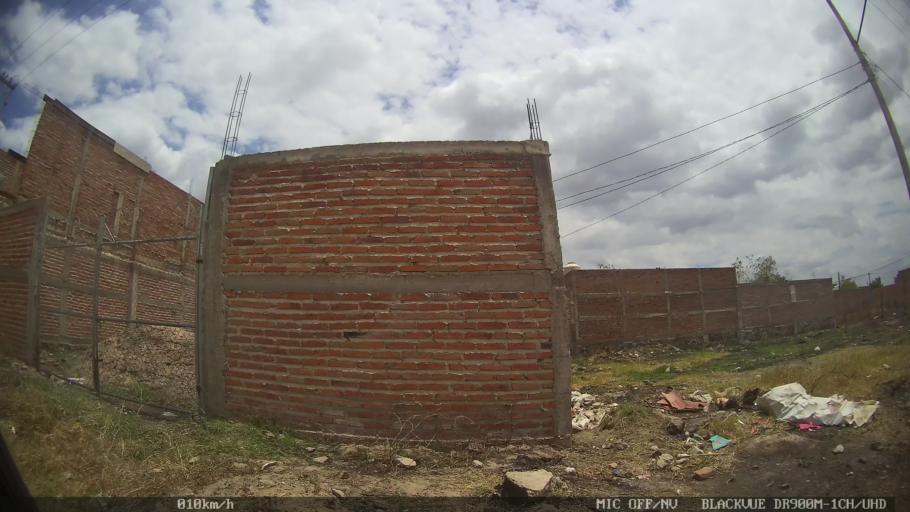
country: MX
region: Jalisco
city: Tlaquepaque
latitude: 20.6414
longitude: -103.2678
